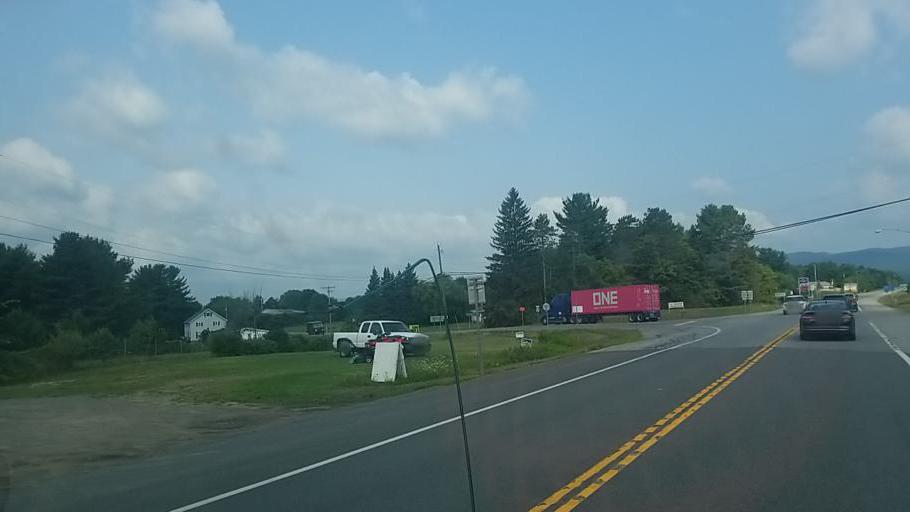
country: US
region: New York
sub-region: Fulton County
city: Broadalbin
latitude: 43.0763
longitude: -74.2588
